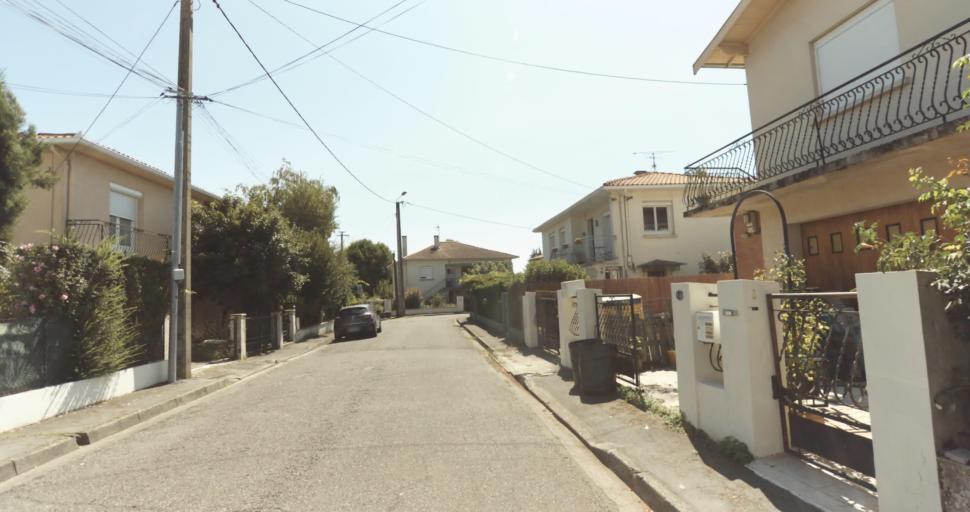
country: FR
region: Midi-Pyrenees
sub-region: Departement de la Haute-Garonne
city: L'Union
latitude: 43.6551
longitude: 1.4794
